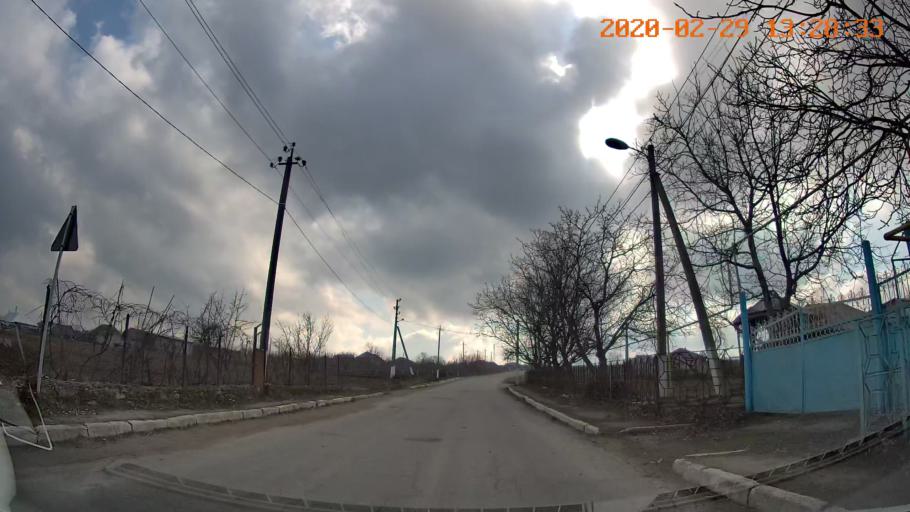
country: MD
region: Telenesti
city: Camenca
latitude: 47.9044
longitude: 28.6422
